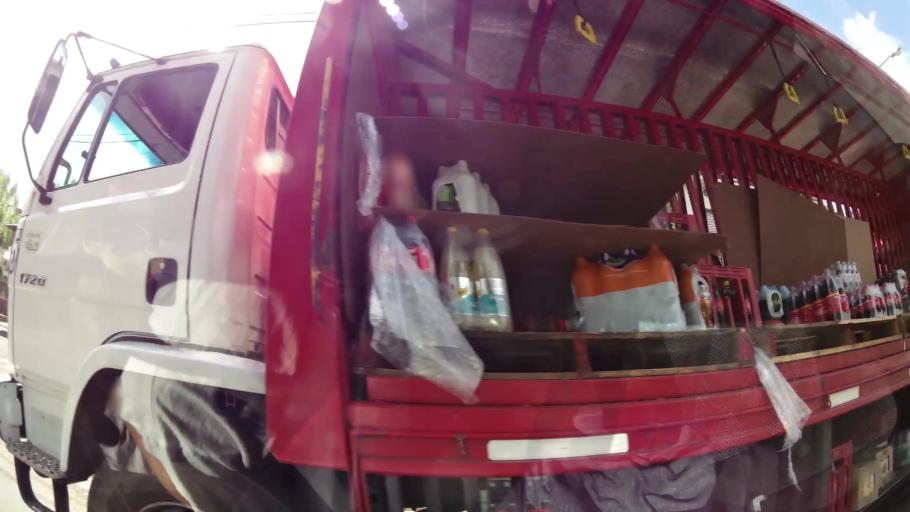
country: AR
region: Buenos Aires
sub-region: Partido de Quilmes
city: Quilmes
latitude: -34.8297
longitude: -58.1835
